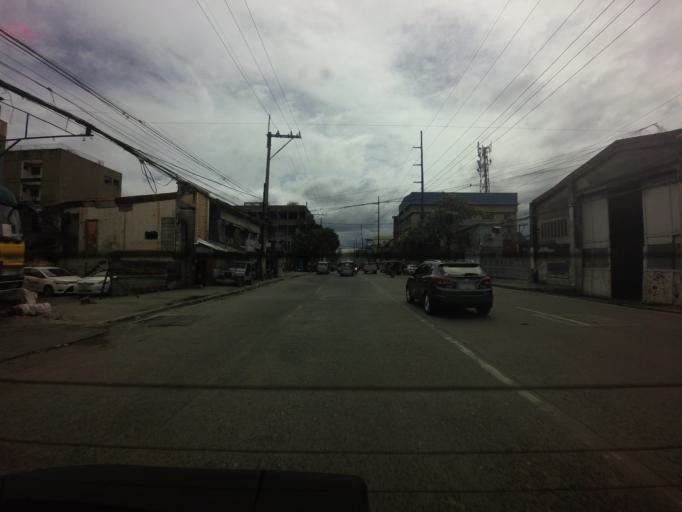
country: PH
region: Metro Manila
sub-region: City of Manila
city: Manila
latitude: 14.6304
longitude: 120.9644
